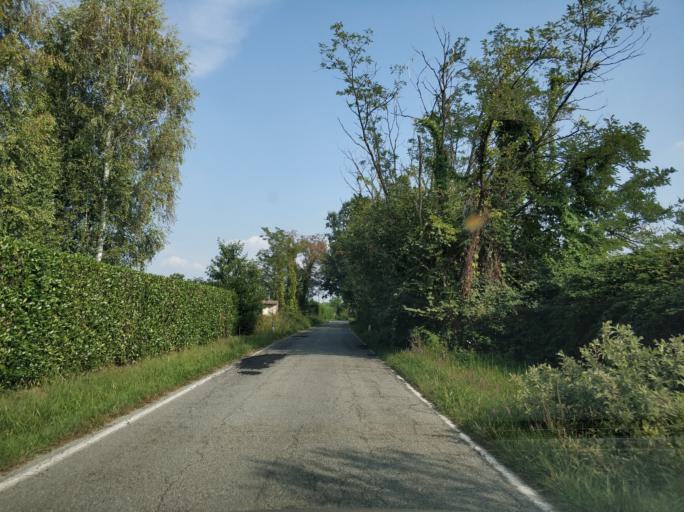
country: IT
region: Piedmont
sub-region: Provincia di Torino
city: San Maurizio
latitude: 45.2384
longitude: 7.6283
